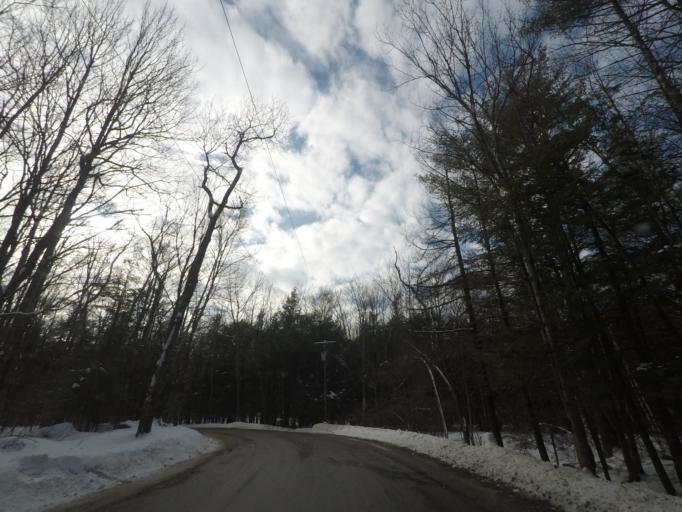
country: US
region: New York
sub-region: Rensselaer County
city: Averill Park
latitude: 42.6283
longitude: -73.5016
